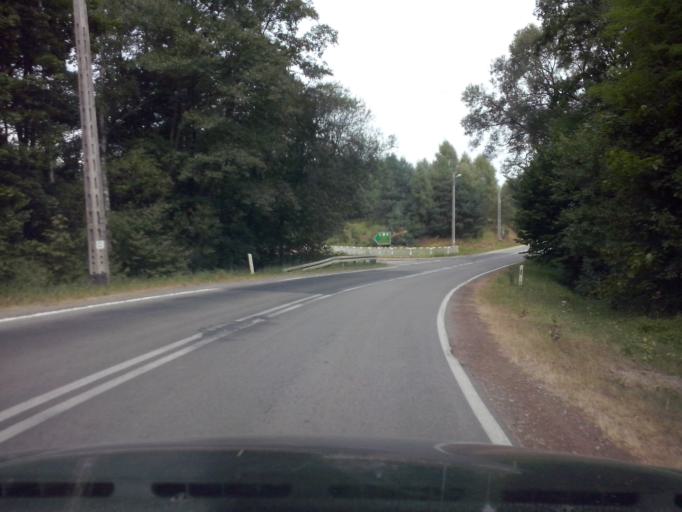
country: PL
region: Swietokrzyskie
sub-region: Powiat kielecki
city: Rakow
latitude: 50.7018
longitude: 21.0553
